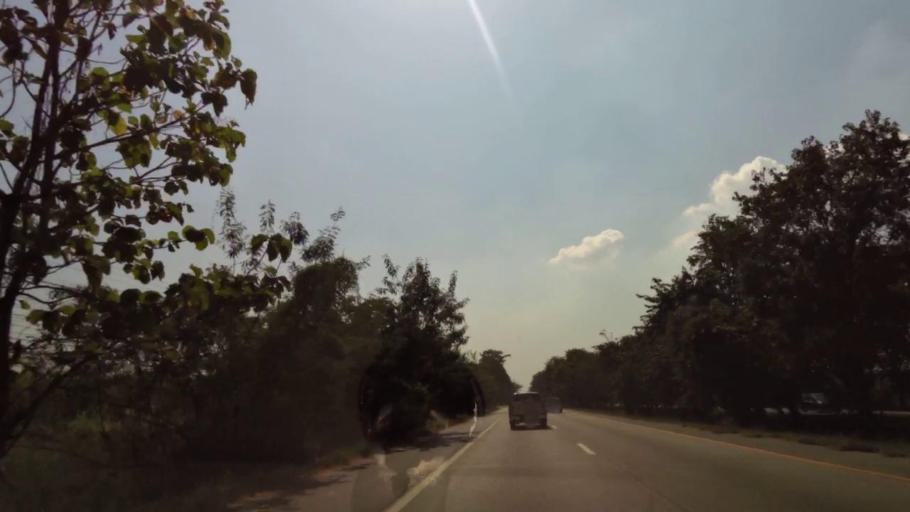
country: TH
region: Phichit
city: Wachira Barami
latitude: 16.5591
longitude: 100.1480
